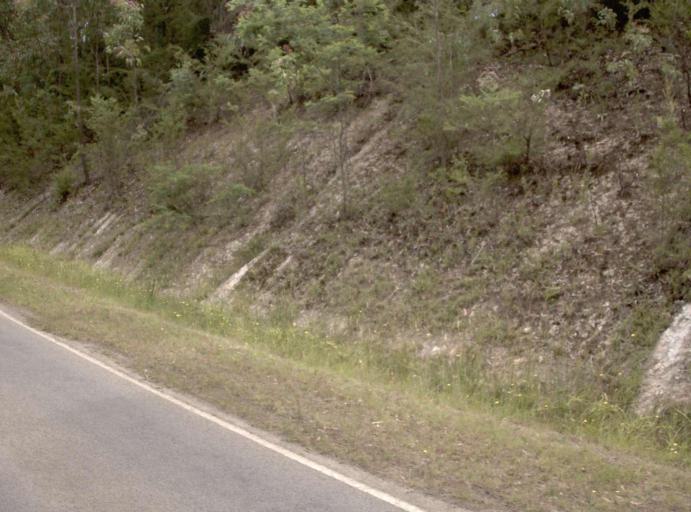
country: AU
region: Victoria
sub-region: Latrobe
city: Traralgon
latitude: -38.0832
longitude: 146.4346
